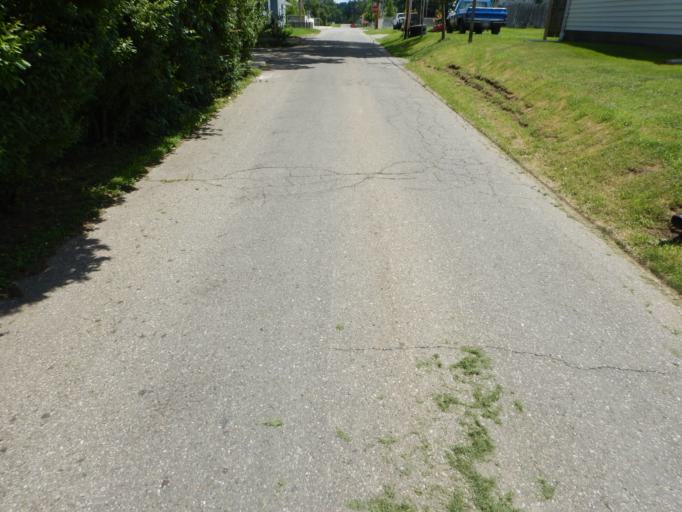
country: US
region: Ohio
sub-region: Muskingum County
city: Zanesville
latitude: 39.9215
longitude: -82.0175
